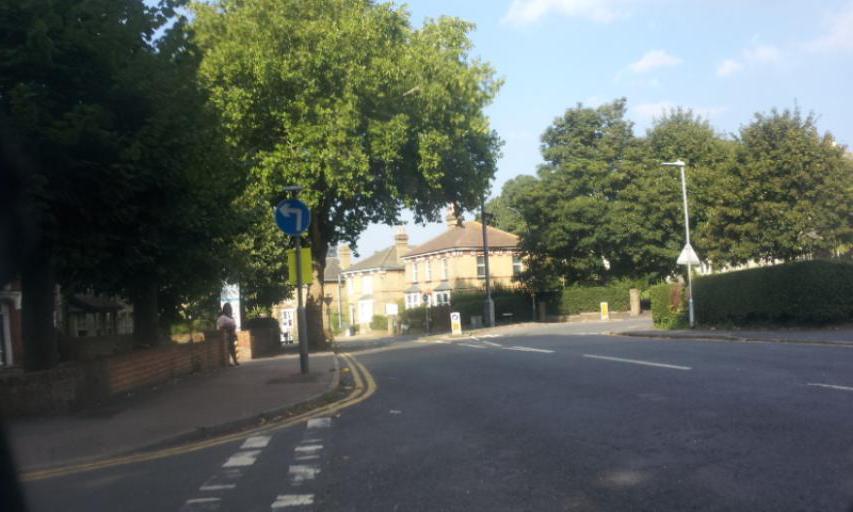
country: GB
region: England
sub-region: Kent
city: Maidstone
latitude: 51.2680
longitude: 0.5222
